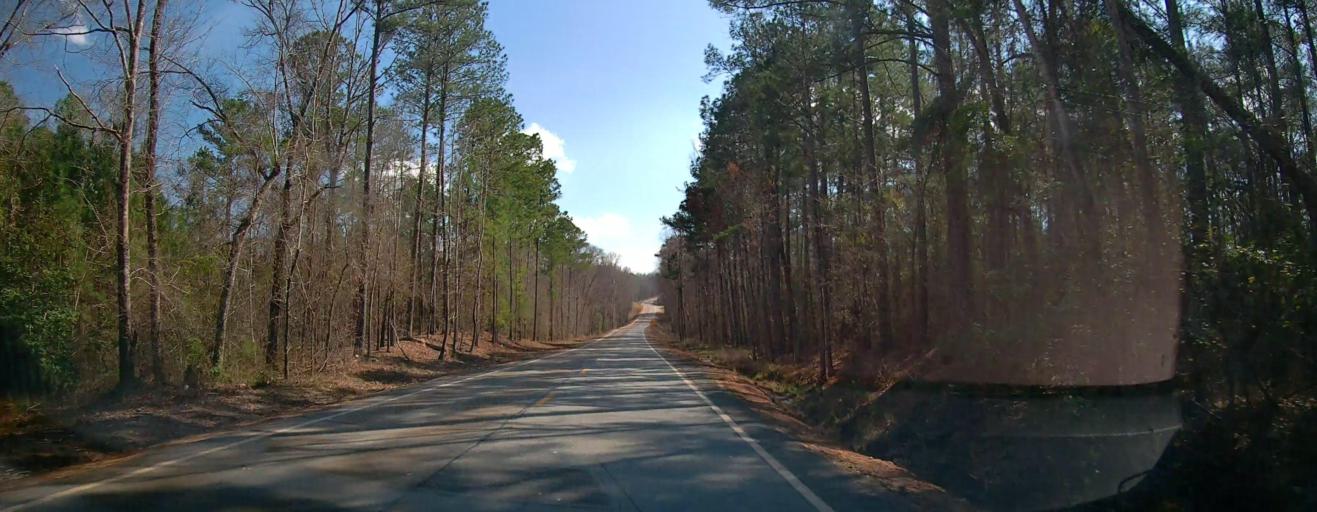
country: US
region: Georgia
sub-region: Wilkinson County
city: Gordon
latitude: 32.8183
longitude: -83.3247
